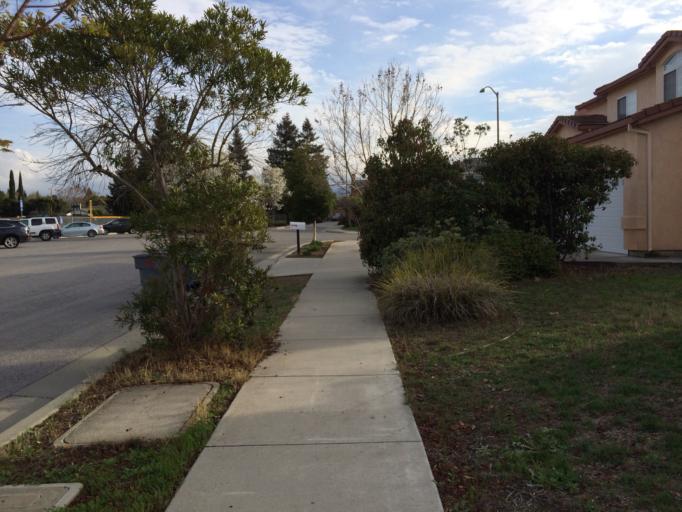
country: US
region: California
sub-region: Santa Clara County
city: Cupertino
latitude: 37.3195
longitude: -122.0221
